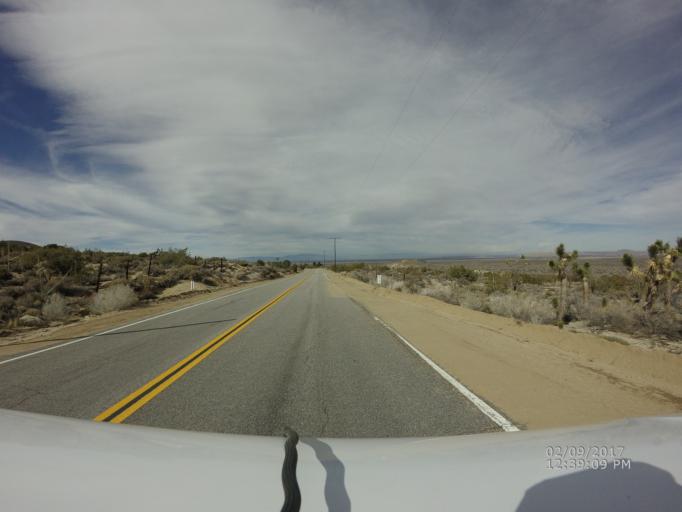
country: US
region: California
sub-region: Los Angeles County
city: Littlerock
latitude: 34.4802
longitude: -117.8644
